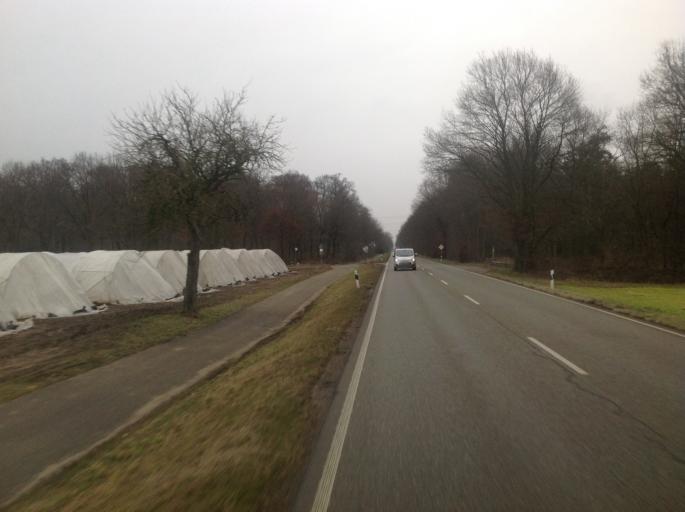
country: DE
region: Baden-Wuerttemberg
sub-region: Karlsruhe Region
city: Iffezheim
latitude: 48.8264
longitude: 8.1677
